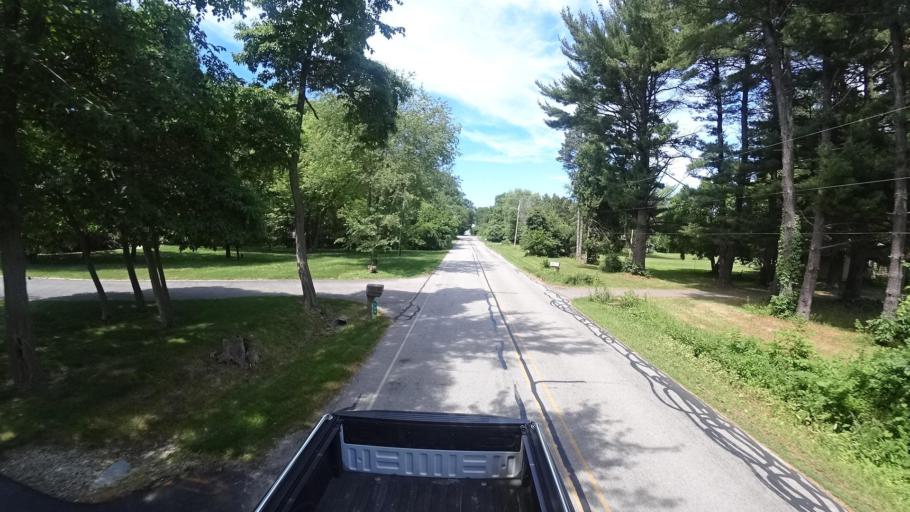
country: US
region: Indiana
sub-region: Porter County
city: Porter
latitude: 41.6259
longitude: -87.0770
